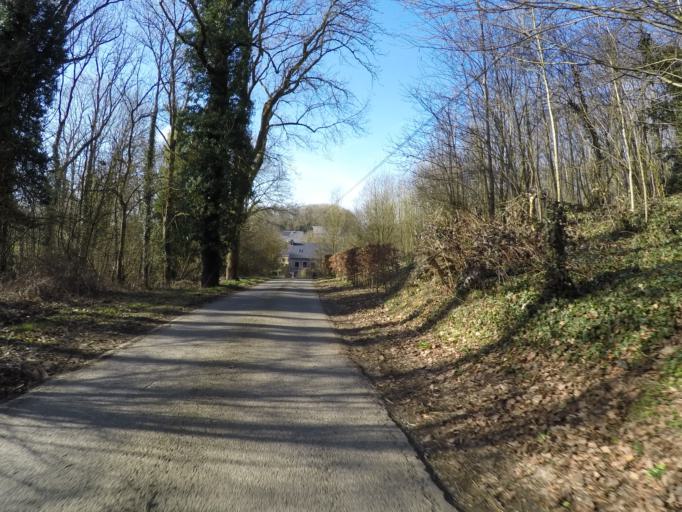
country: BE
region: Wallonia
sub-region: Province de Namur
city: Gesves
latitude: 50.3576
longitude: 5.0875
